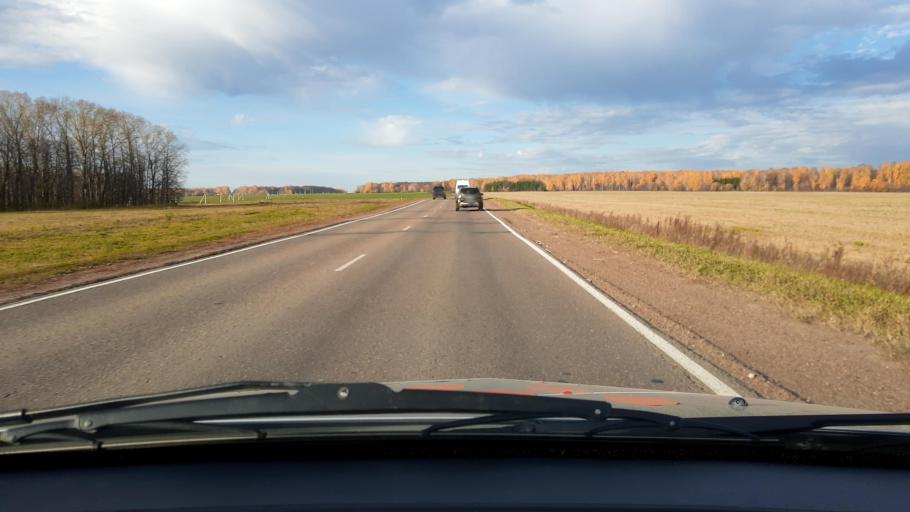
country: RU
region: Bashkortostan
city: Mikhaylovka
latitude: 54.8225
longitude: 55.7556
